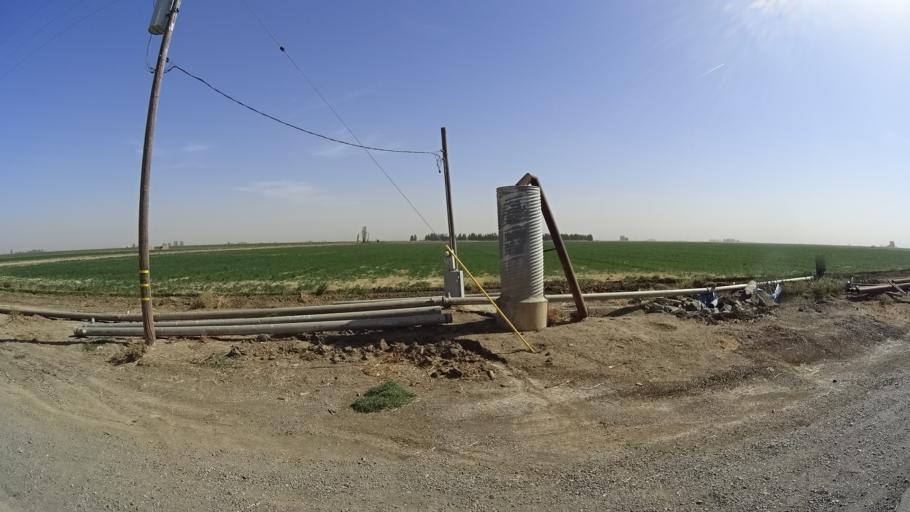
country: US
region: California
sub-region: Yolo County
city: Davis
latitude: 38.4658
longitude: -121.6937
